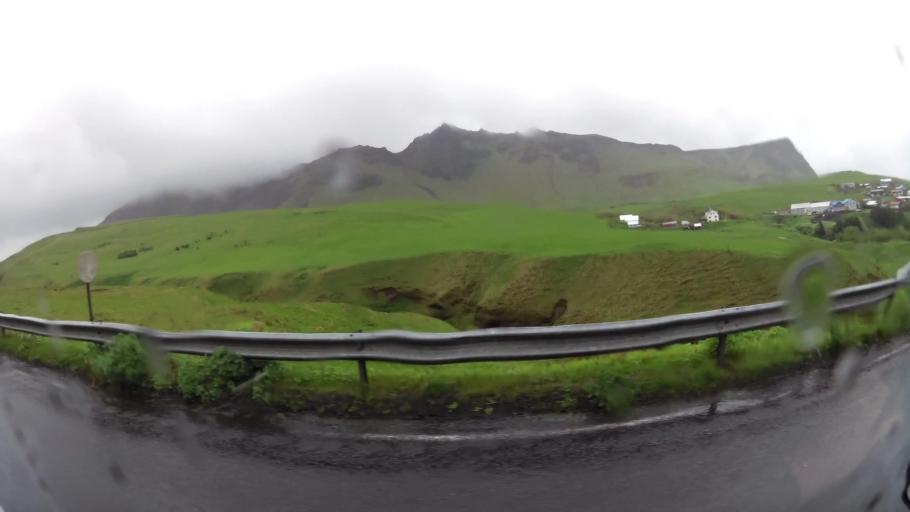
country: IS
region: South
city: Vestmannaeyjar
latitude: 63.4228
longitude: -19.0153
